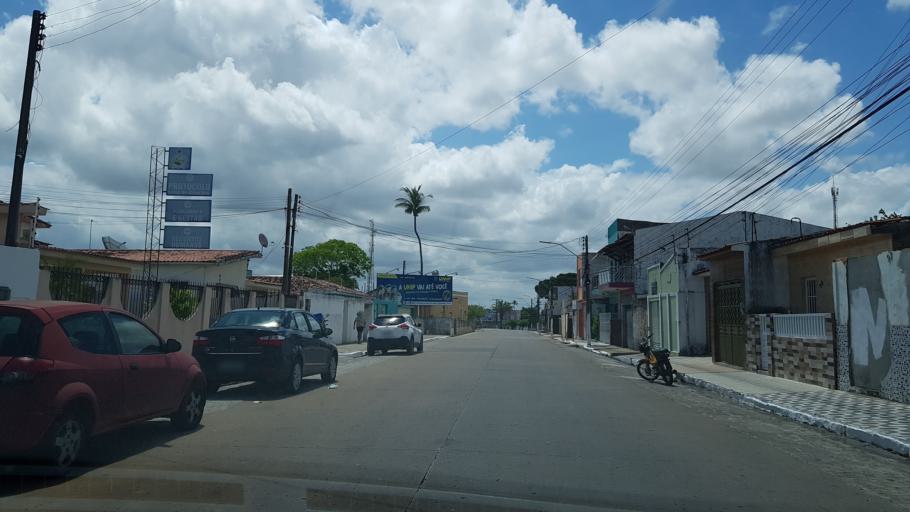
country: BR
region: Alagoas
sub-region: Penedo
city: Penedo
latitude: -10.2825
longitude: -36.5661
